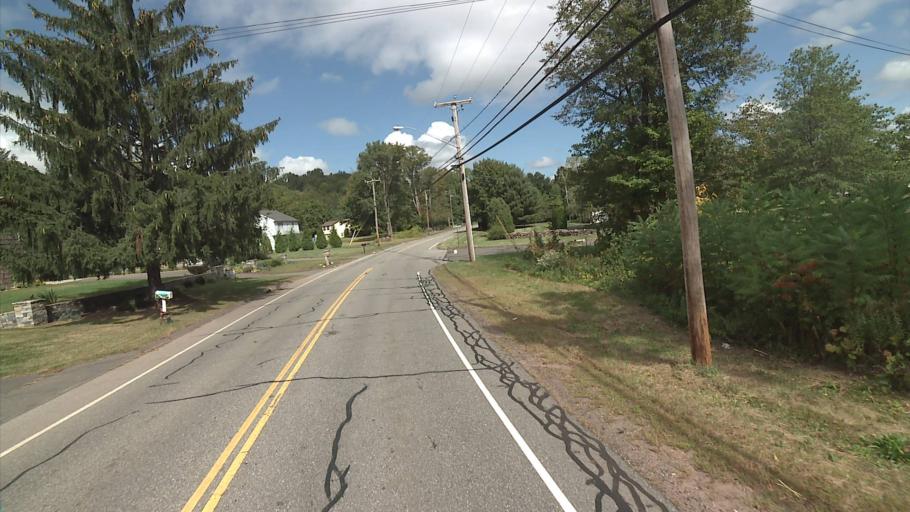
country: US
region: Connecticut
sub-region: Middlesex County
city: Durham
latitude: 41.5064
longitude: -72.7169
